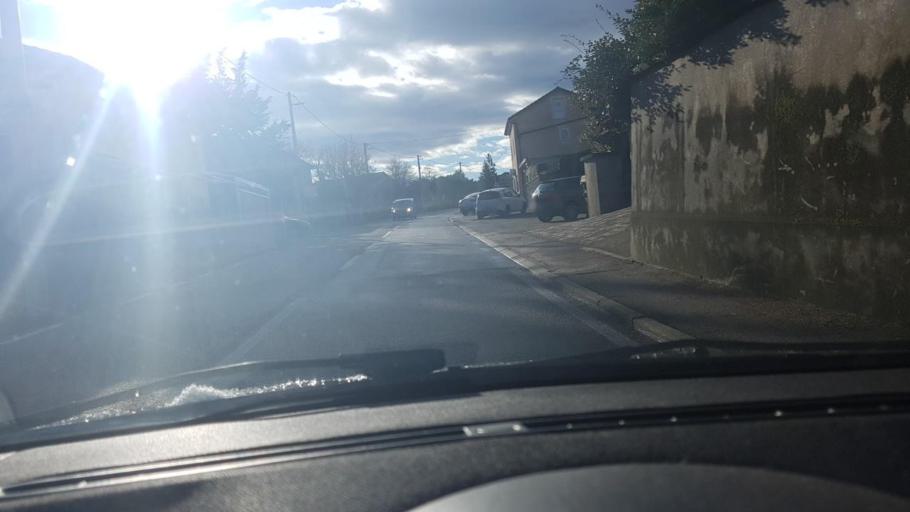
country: HR
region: Primorsko-Goranska
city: Cavle
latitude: 45.3533
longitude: 14.4859
